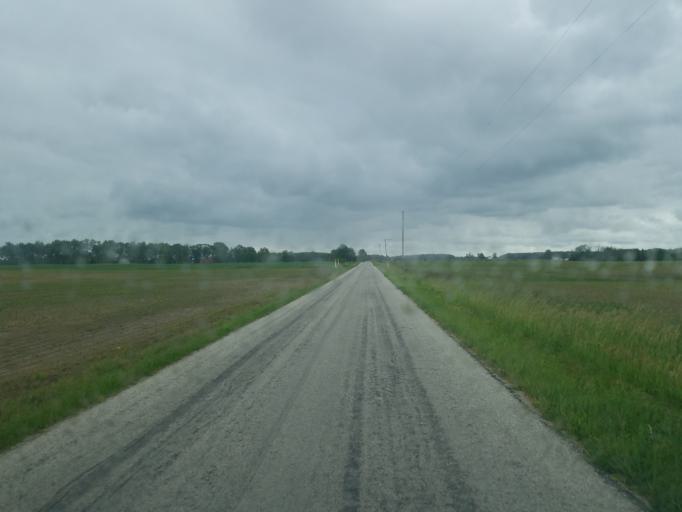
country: US
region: Ohio
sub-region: Morrow County
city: Cardington
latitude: 40.5365
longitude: -82.9006
